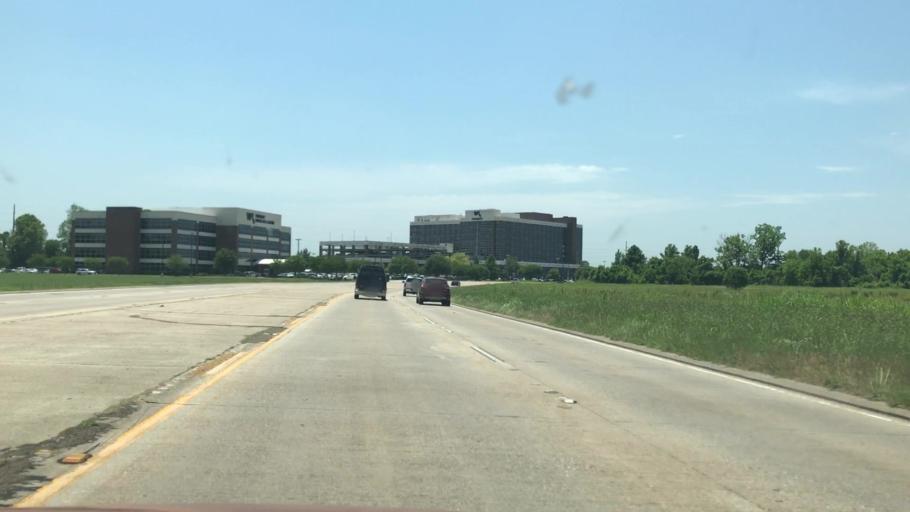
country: US
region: Louisiana
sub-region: Bossier Parish
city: Bossier City
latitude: 32.4364
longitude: -93.7073
